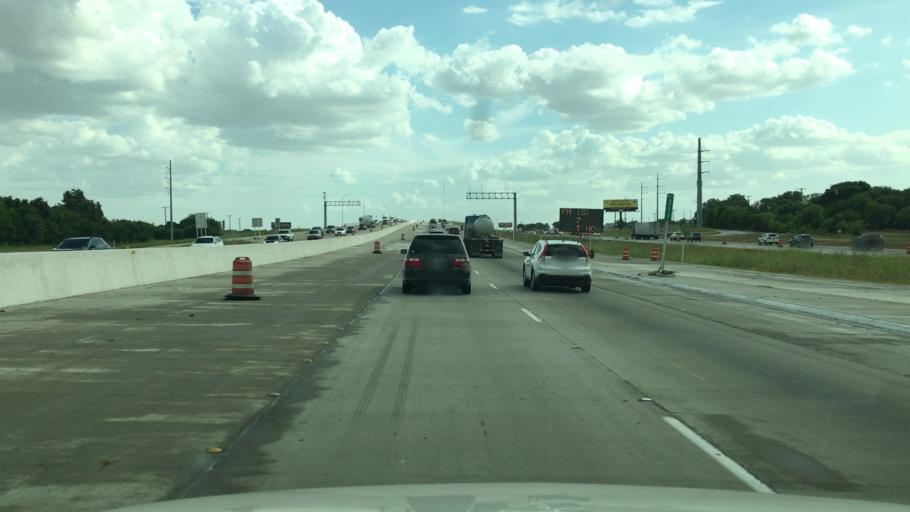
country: US
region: Texas
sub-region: McLennan County
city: Bruceville-Eddy
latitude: 31.3124
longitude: -97.2417
